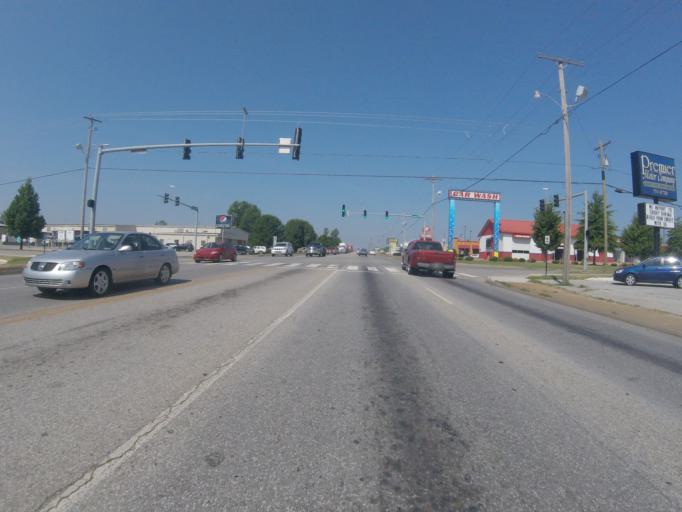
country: US
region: Arkansas
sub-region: Washington County
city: Springdale
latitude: 36.1671
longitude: -94.1255
